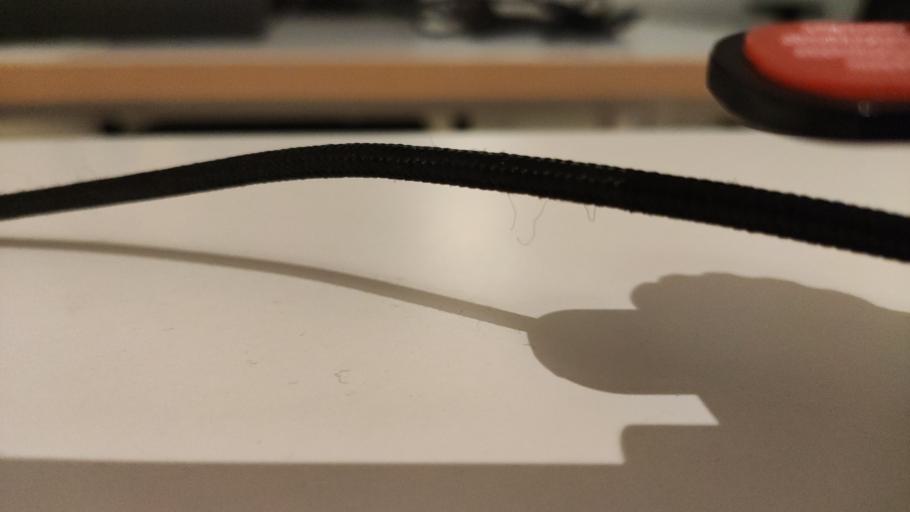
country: RU
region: Moskovskaya
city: Il'inskiy Pogost
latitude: 55.5334
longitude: 38.8726
